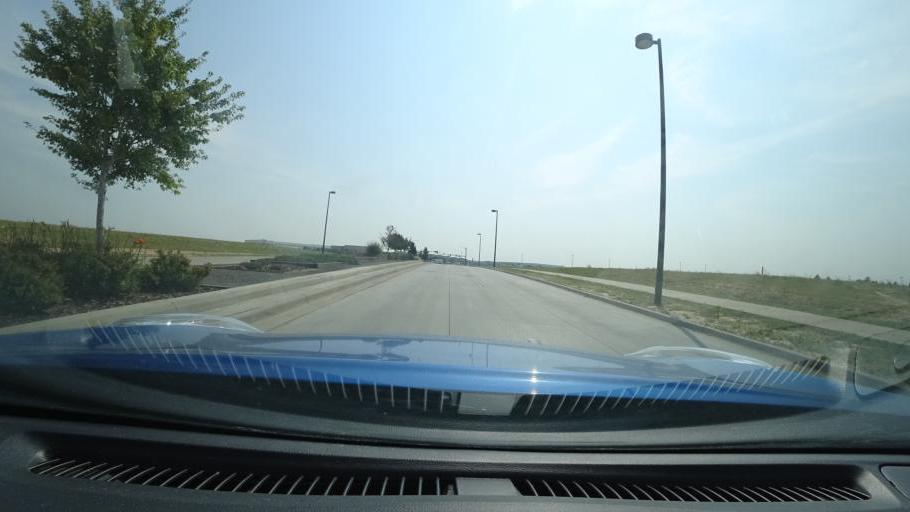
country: US
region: Colorado
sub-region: Adams County
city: Aurora
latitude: 39.7728
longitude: -104.7864
